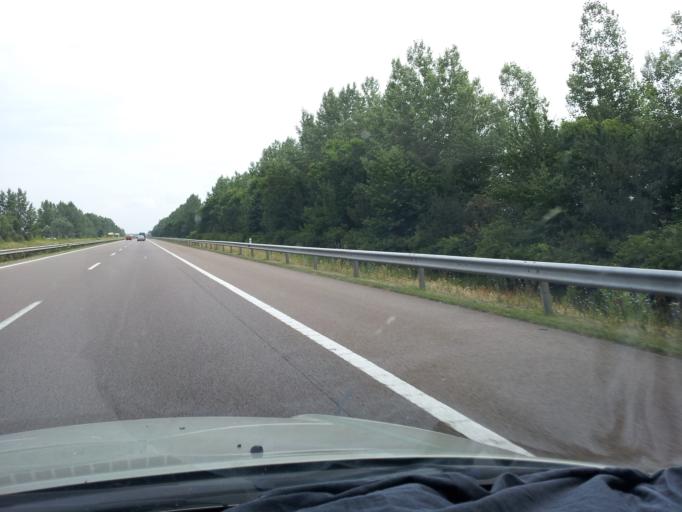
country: HU
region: Borsod-Abauj-Zemplen
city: Mezokovesd
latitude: 47.7847
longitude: 20.6071
